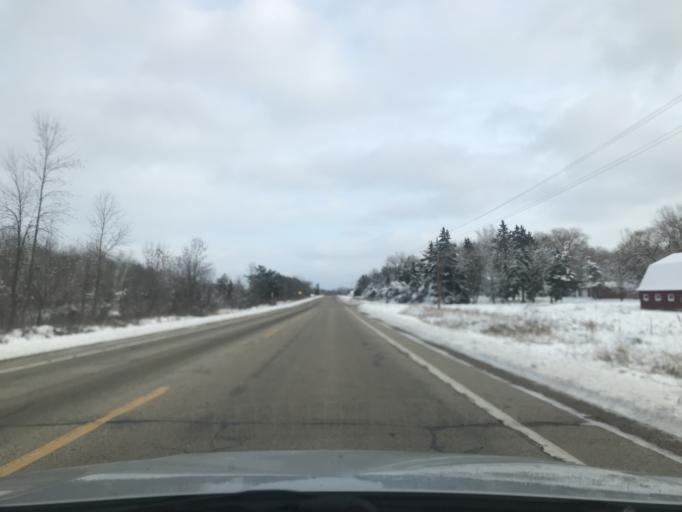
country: US
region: Wisconsin
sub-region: Oconto County
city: Oconto Falls
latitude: 44.8870
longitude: -88.0281
